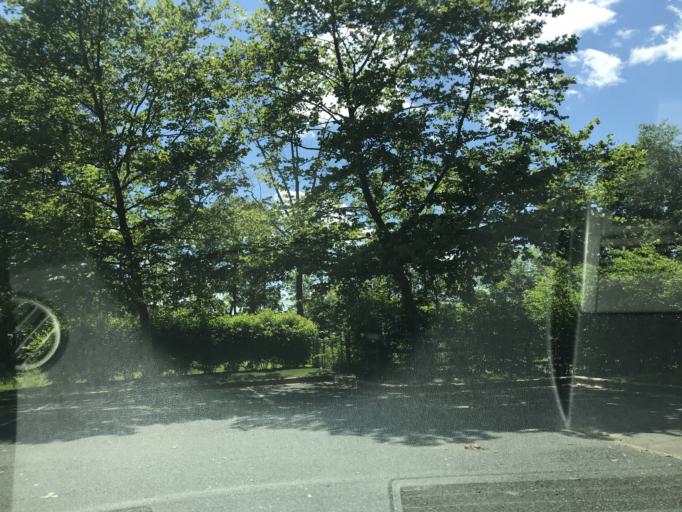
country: US
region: Maryland
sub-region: Harford County
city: Bel Air
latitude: 39.5281
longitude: -76.3482
